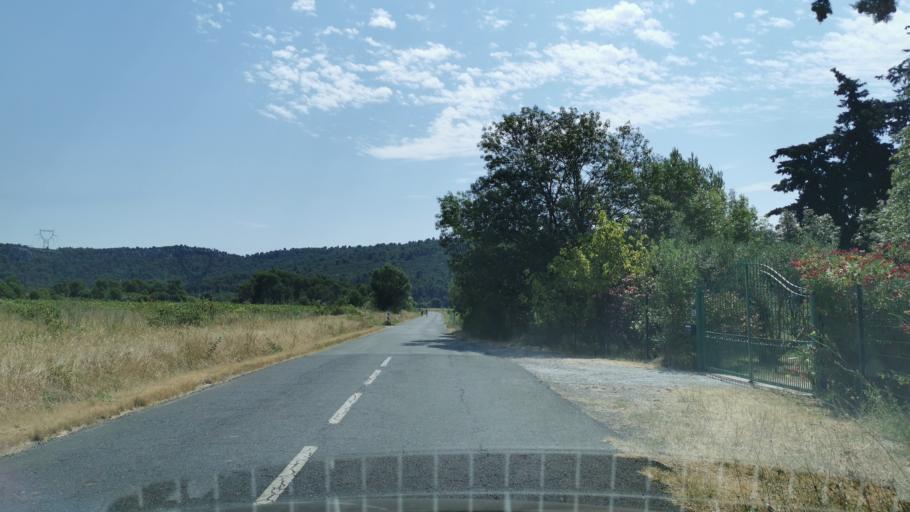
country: FR
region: Languedoc-Roussillon
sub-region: Departement de l'Aude
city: Bize-Minervois
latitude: 43.3427
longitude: 2.8708
